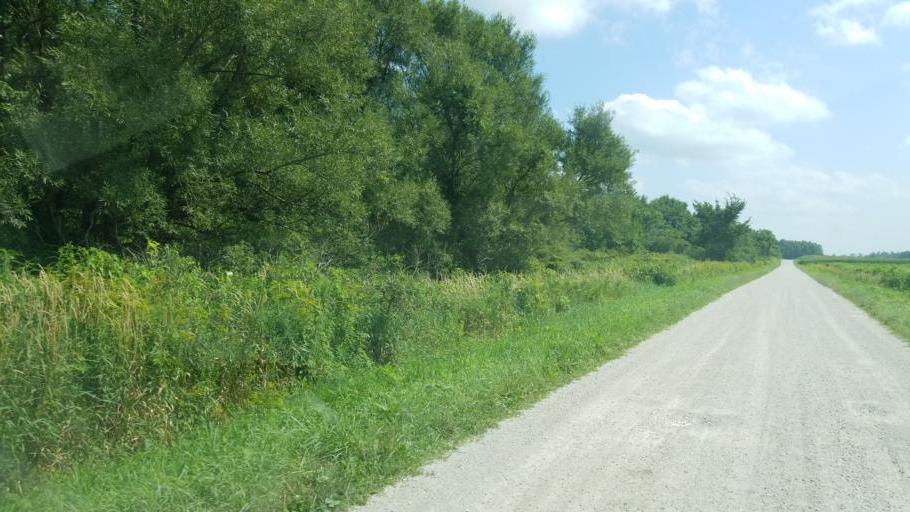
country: US
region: Ohio
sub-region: Huron County
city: Willard
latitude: 41.0014
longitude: -82.7804
